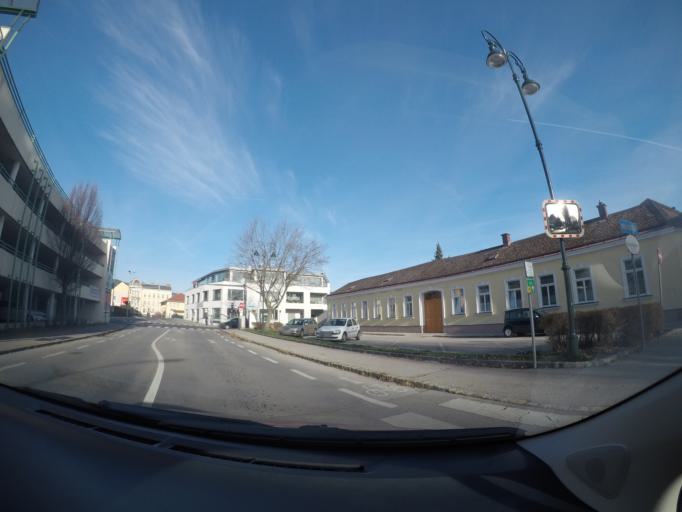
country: AT
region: Lower Austria
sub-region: Politischer Bezirk Baden
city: Baden
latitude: 48.0028
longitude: 16.2370
